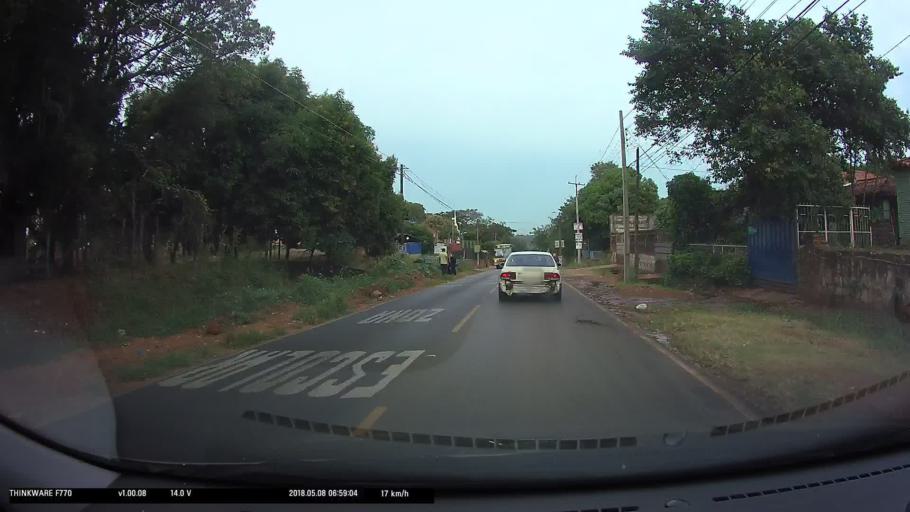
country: PY
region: Central
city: Limpio
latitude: -25.2461
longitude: -57.4828
